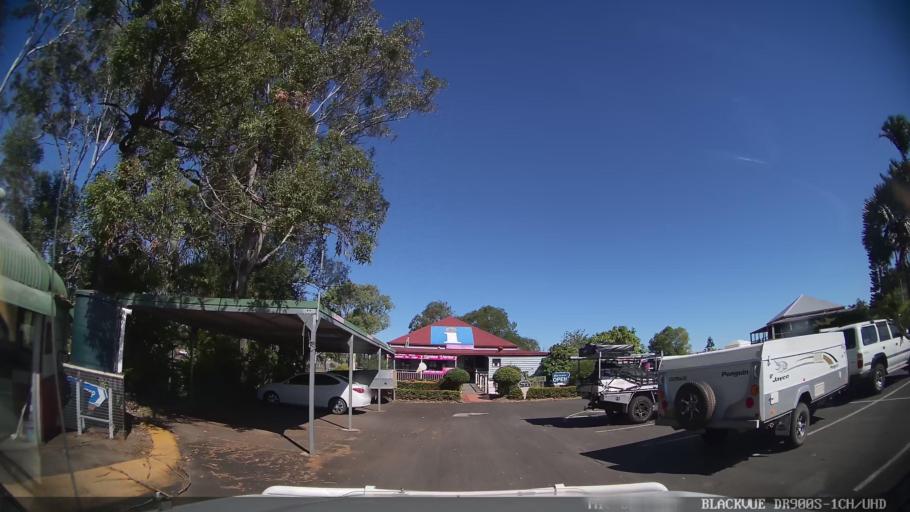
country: AU
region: Queensland
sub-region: Fraser Coast
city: Maryborough
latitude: -25.5770
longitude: 152.6546
